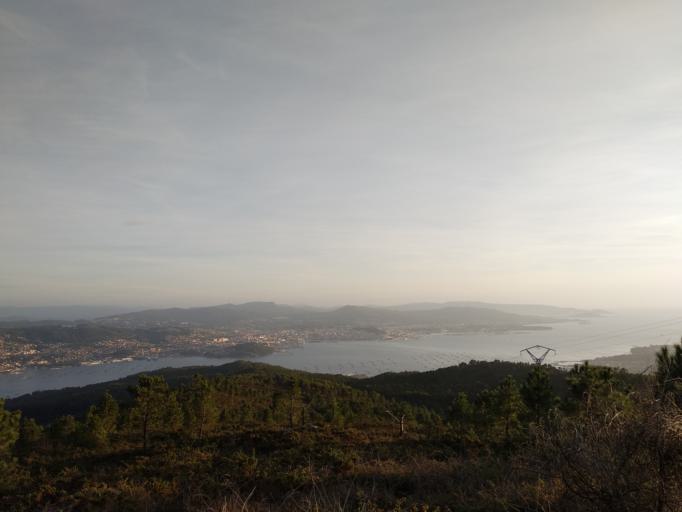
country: ES
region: Galicia
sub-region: Provincia de Pontevedra
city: Moana
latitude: 42.3148
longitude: -8.7040
